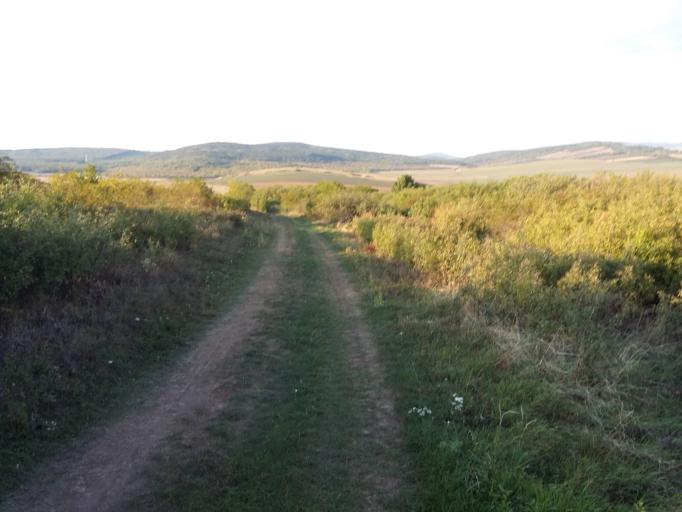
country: HU
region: Borsod-Abauj-Zemplen
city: Bekecs
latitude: 48.1587
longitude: 21.1731
